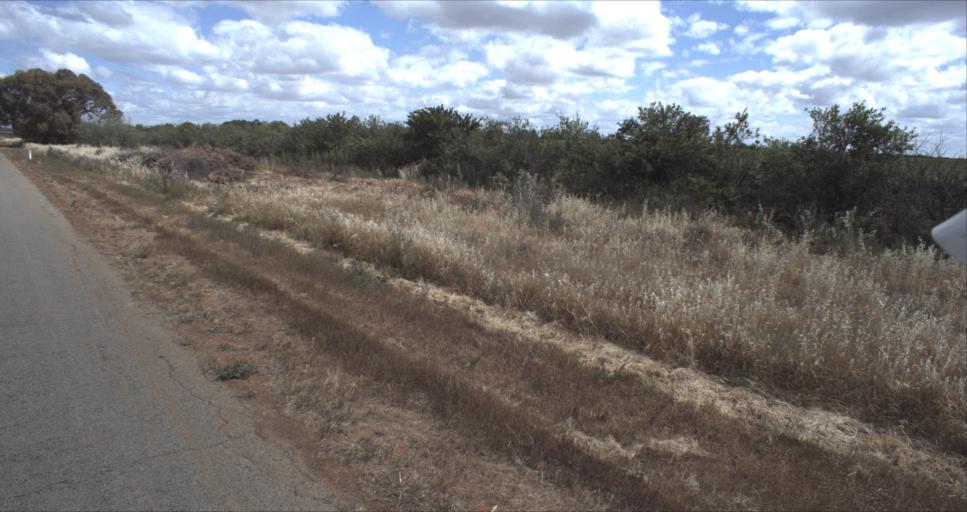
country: AU
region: New South Wales
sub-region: Leeton
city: Leeton
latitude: -34.5858
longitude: 146.3961
